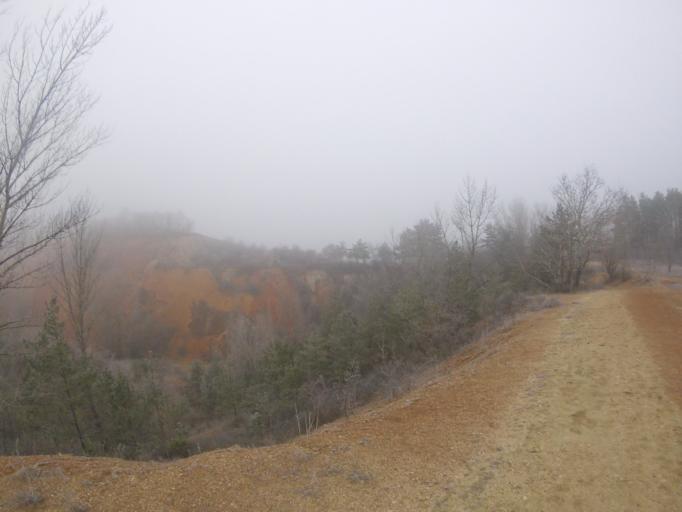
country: HU
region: Fejer
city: Zamoly
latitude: 47.3670
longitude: 18.3870
